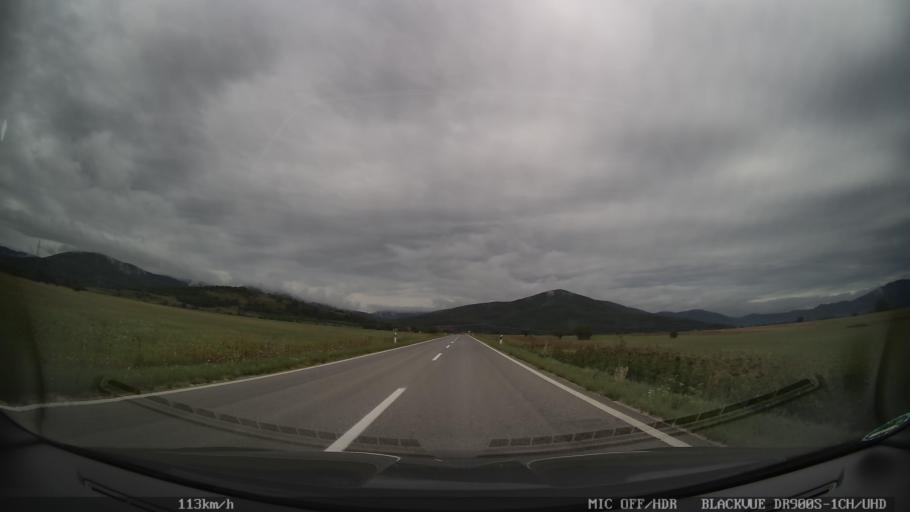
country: HR
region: Licko-Senjska
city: Otocac
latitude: 44.8594
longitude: 15.3142
